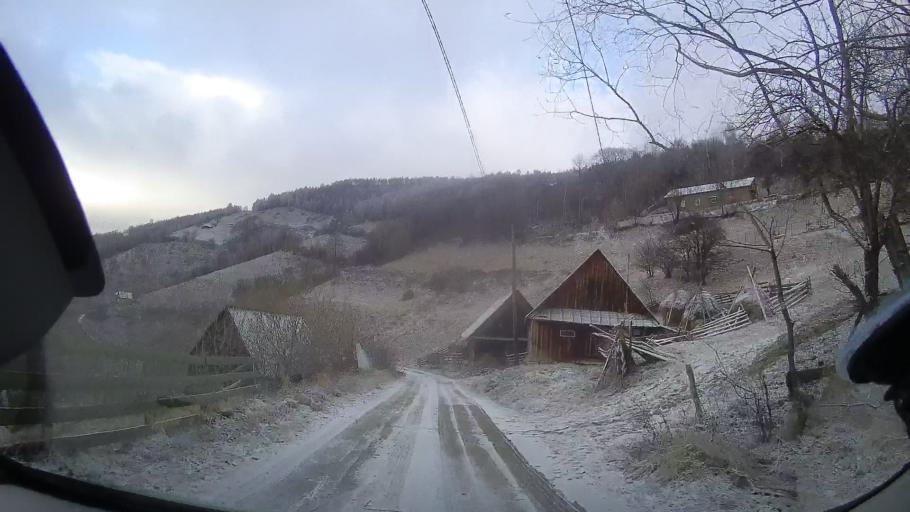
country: RO
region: Cluj
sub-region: Comuna Valea Ierii
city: Valea Ierii
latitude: 46.6669
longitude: 23.3316
